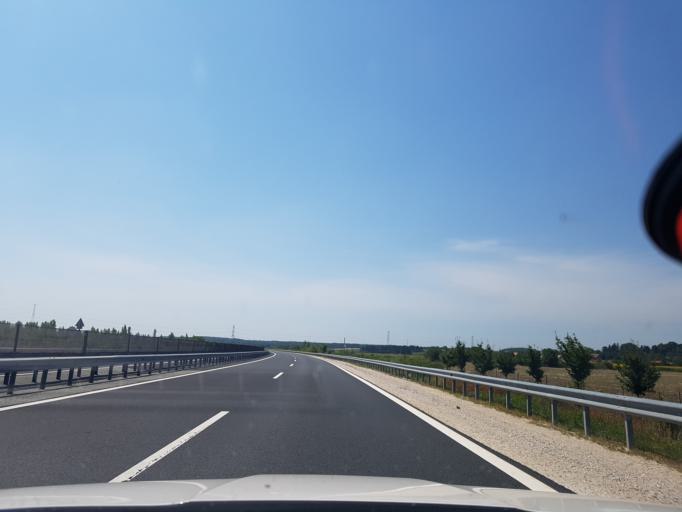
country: HU
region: Vas
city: Sarvar
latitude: 47.3117
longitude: 16.8393
